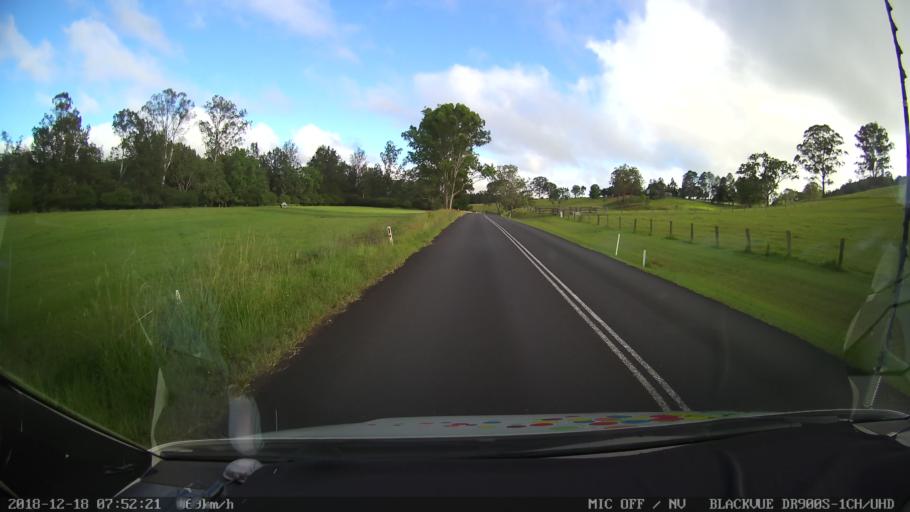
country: AU
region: New South Wales
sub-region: Kyogle
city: Kyogle
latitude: -28.4294
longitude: 152.5809
